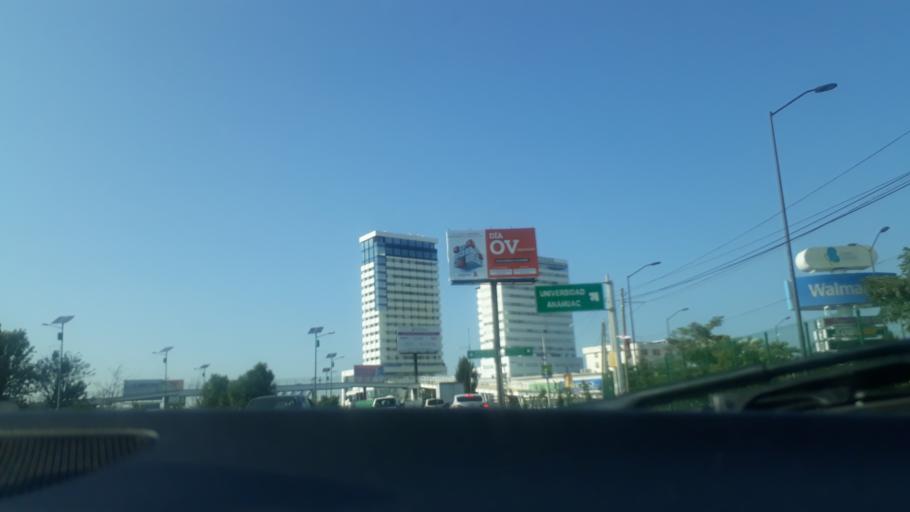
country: MX
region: Puebla
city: Tlazcalancingo
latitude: 19.0173
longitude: -98.2644
